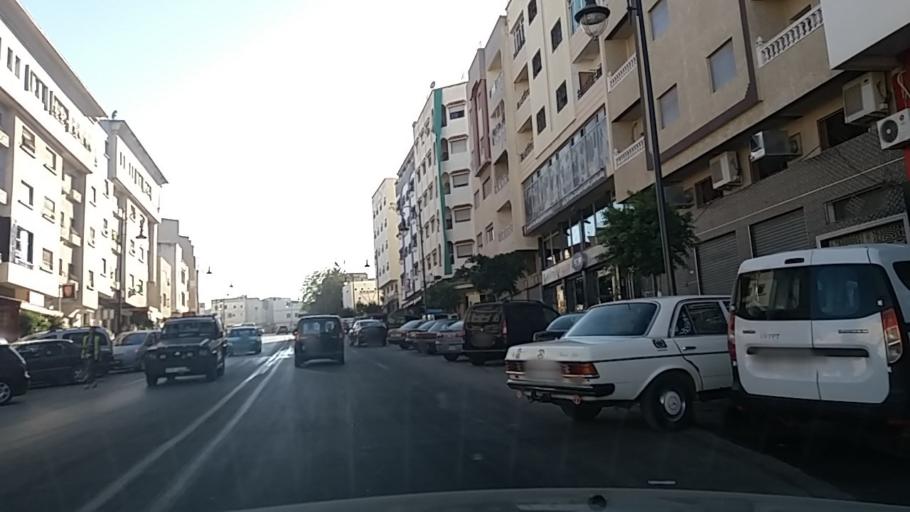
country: MA
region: Tanger-Tetouan
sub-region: Tanger-Assilah
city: Tangier
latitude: 35.7540
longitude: -5.8180
